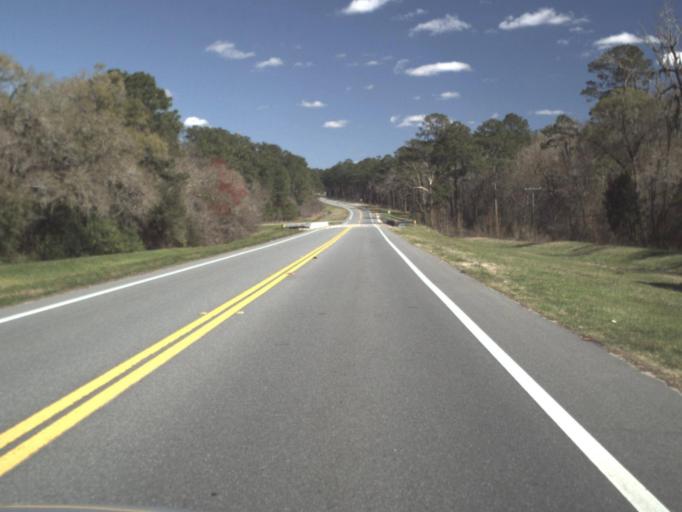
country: US
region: Florida
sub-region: Gadsden County
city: Chattahoochee
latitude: 30.7011
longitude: -84.8282
